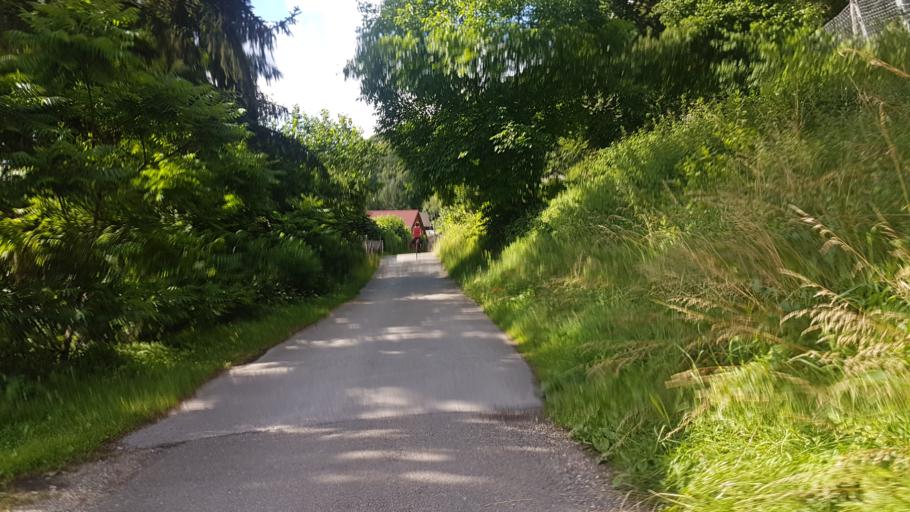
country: DE
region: Bavaria
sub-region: Upper Bavaria
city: Walting
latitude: 48.9428
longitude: 11.3520
